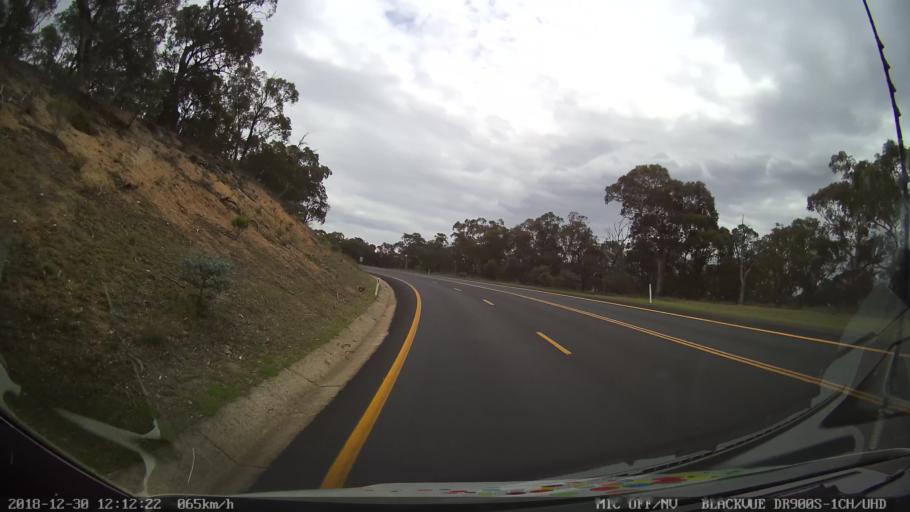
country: AU
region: New South Wales
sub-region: Snowy River
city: Jindabyne
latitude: -36.3580
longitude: 148.5894
